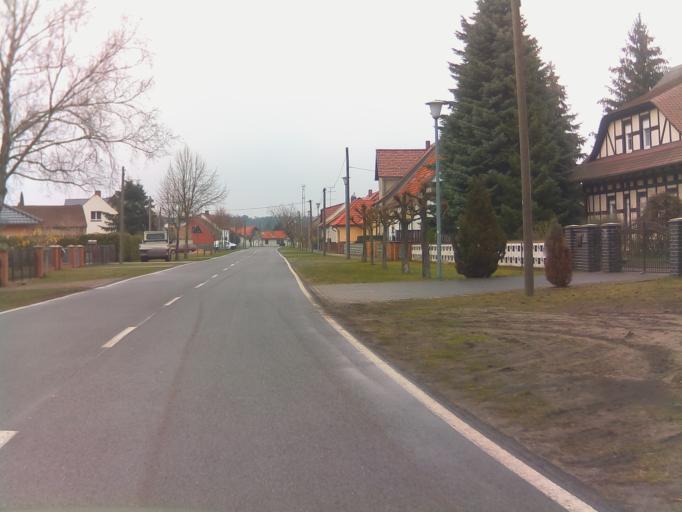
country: DE
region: Brandenburg
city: Schlepzig
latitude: 51.9819
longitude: 13.9710
